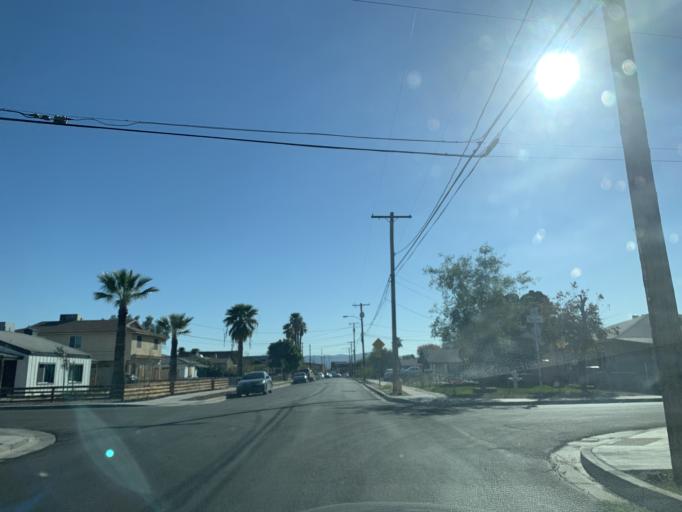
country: US
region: Arizona
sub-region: Maricopa County
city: Phoenix
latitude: 33.4542
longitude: -112.0522
